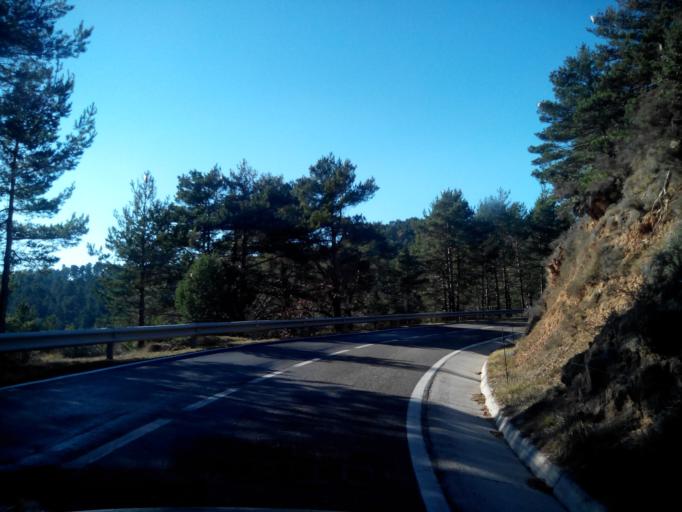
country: ES
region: Catalonia
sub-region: Provincia de Barcelona
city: Castellar del Riu
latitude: 42.0940
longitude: 1.7831
